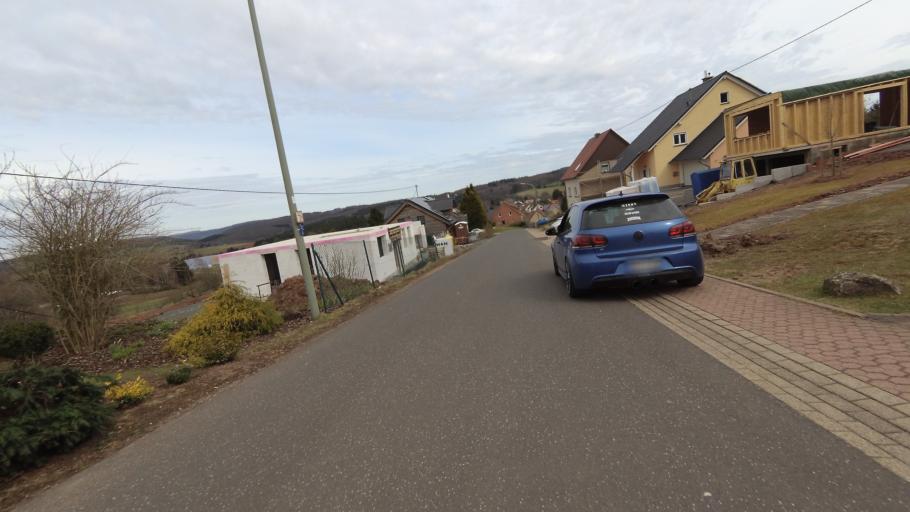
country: DE
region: Saarland
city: Mainzweiler
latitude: 49.4201
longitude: 7.1131
